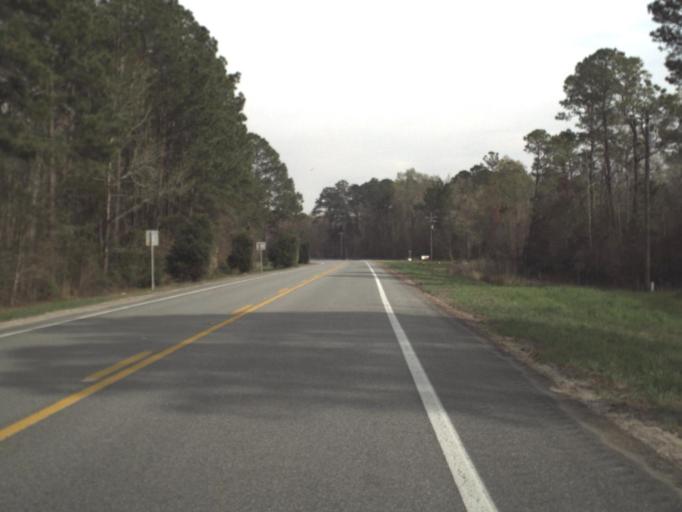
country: US
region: Florida
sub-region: Jefferson County
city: Monticello
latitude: 30.4934
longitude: -83.7352
